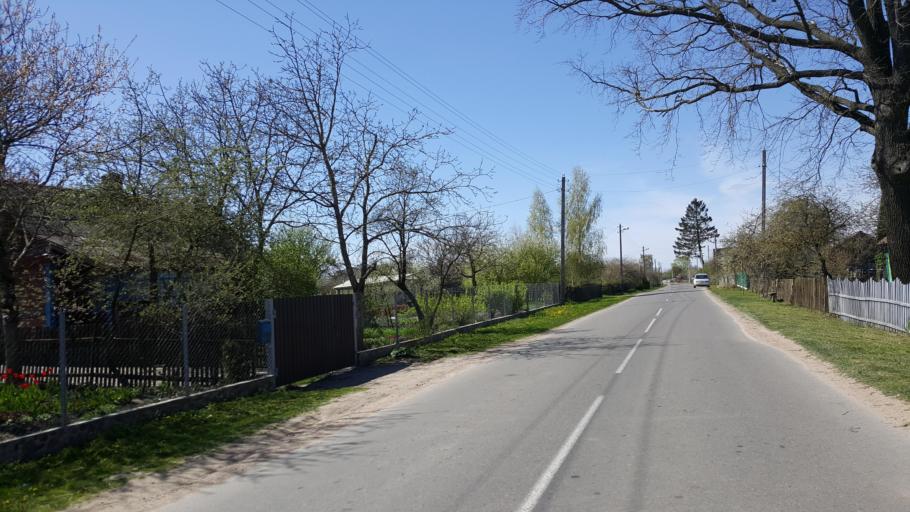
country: BY
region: Brest
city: Vysokaye
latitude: 52.3551
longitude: 23.5171
